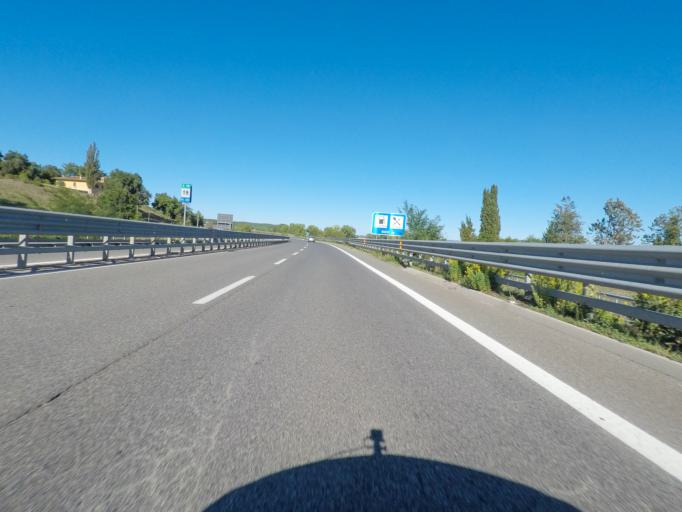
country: IT
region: Tuscany
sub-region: Provincia di Grosseto
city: Campagnatico
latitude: 42.9230
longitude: 11.2633
